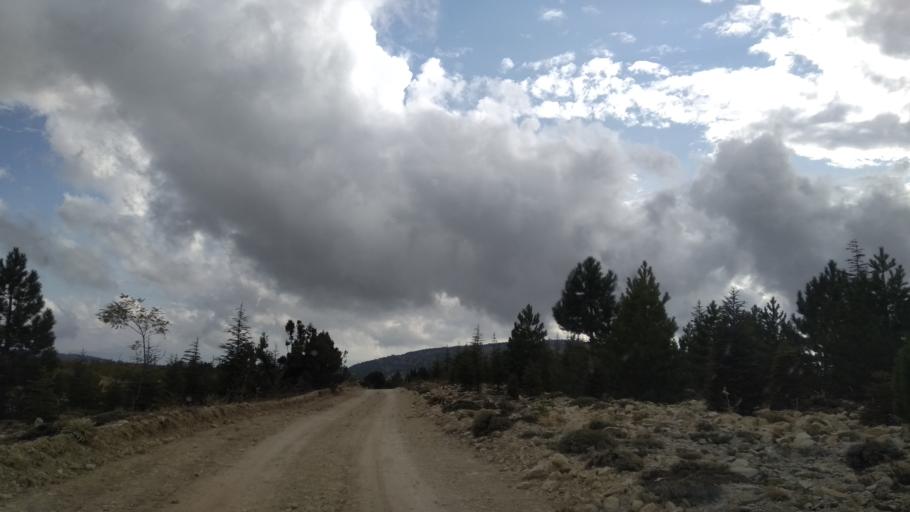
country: TR
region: Mersin
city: Sarikavak
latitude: 36.5720
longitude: 33.7556
